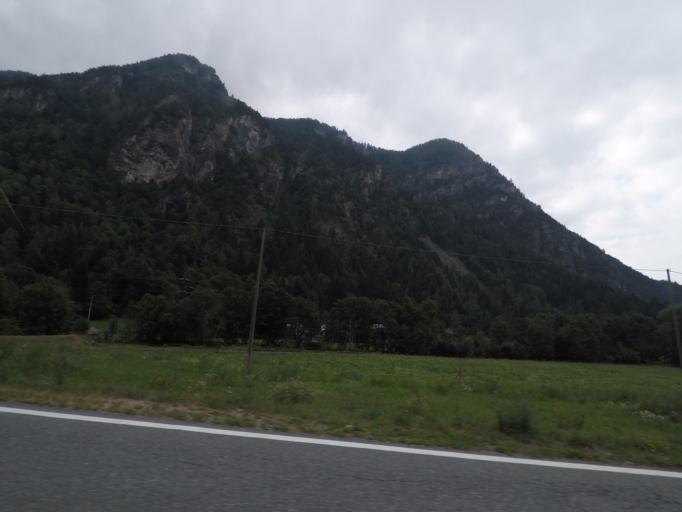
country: IT
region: Aosta Valley
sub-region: Valle d'Aosta
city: Antey-Saint-Andre
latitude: 45.8205
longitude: 7.5898
